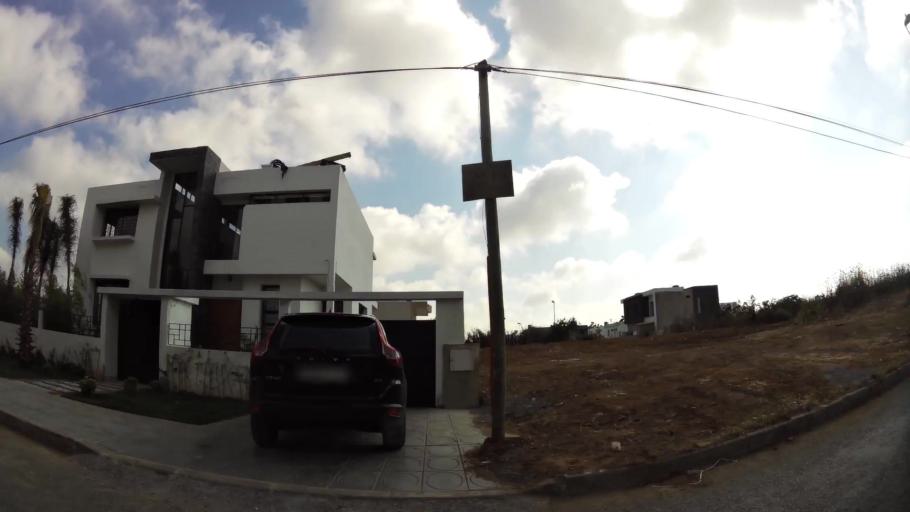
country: MA
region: Rabat-Sale-Zemmour-Zaer
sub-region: Skhirate-Temara
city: Temara
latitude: 33.9531
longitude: -6.8761
